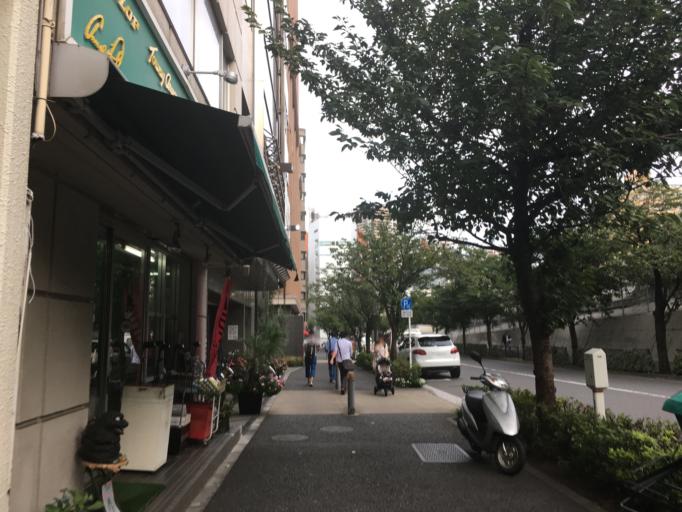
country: JP
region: Tokyo
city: Tokyo
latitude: 35.6282
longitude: 139.7215
